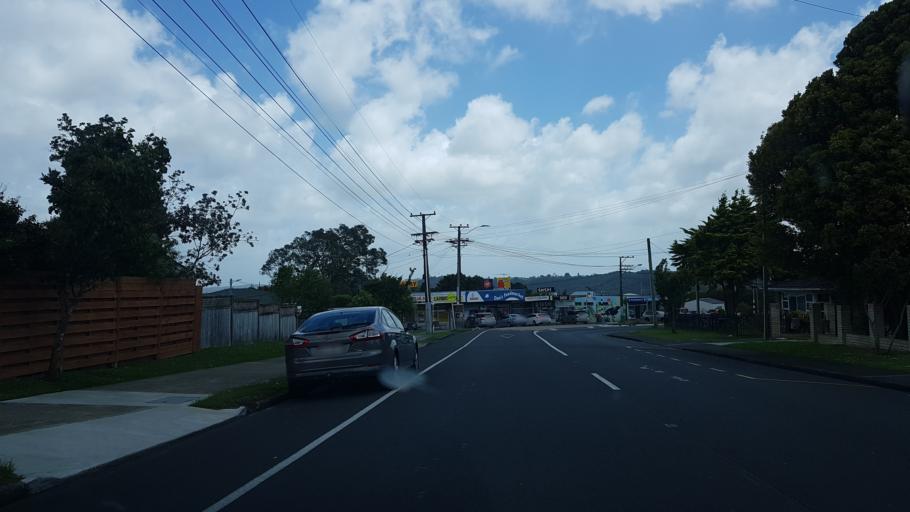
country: NZ
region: Auckland
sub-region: Auckland
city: North Shore
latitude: -36.7991
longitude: 174.7014
